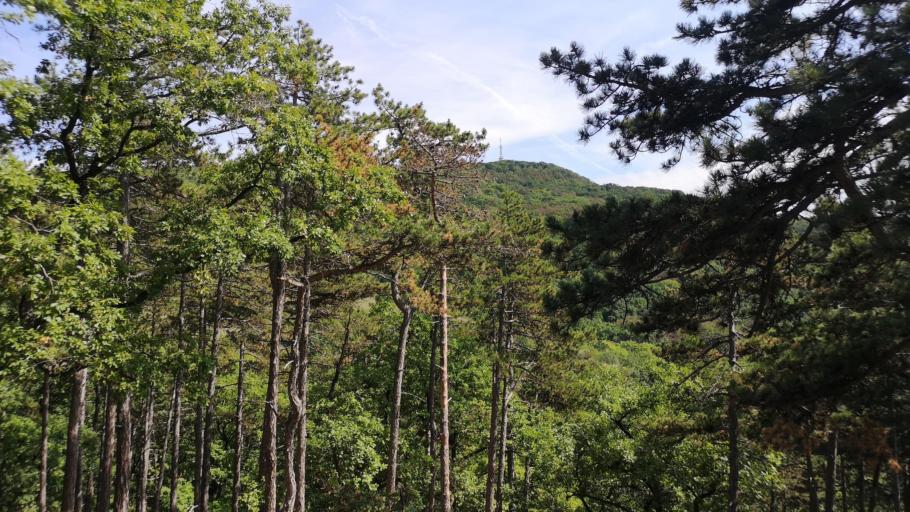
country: SK
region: Nitriansky
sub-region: Okres Nitra
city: Nitra
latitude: 48.3478
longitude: 18.0920
